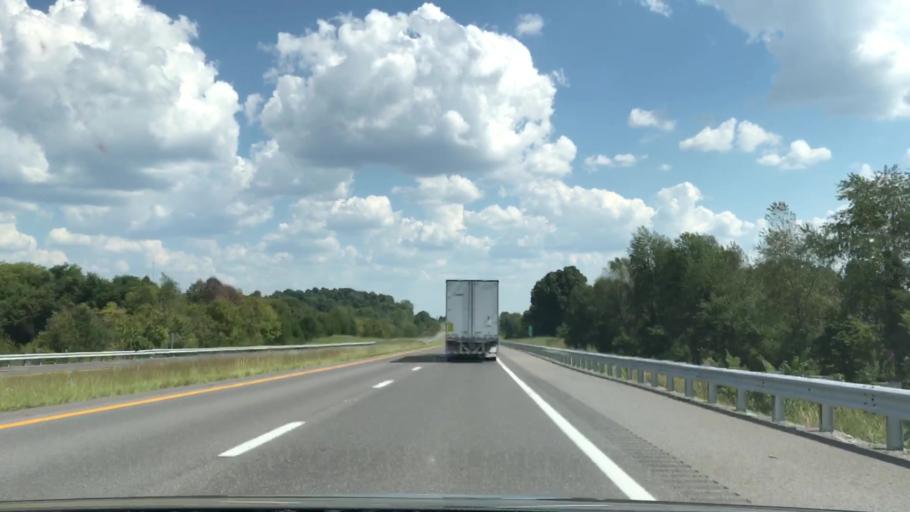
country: US
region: Kentucky
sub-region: Caldwell County
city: Princeton
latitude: 37.1106
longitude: -87.9611
